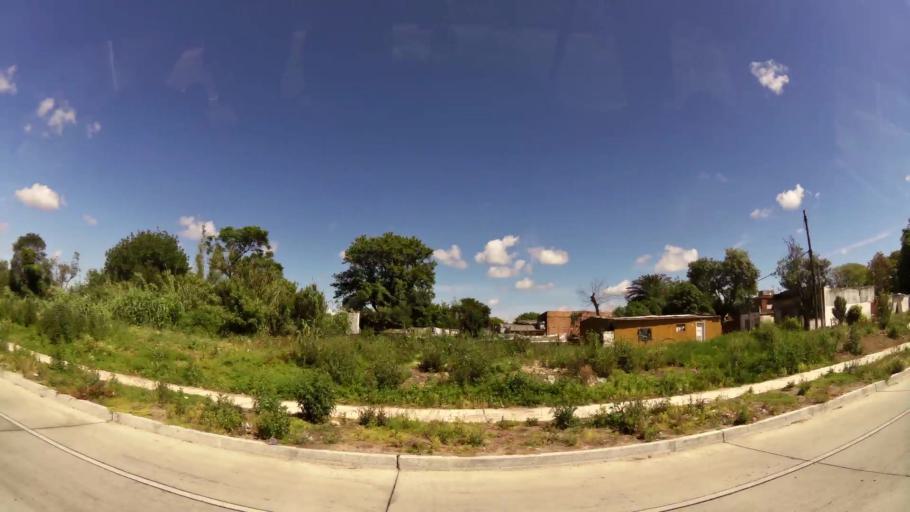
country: UY
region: Montevideo
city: Montevideo
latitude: -34.8471
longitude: -56.1465
